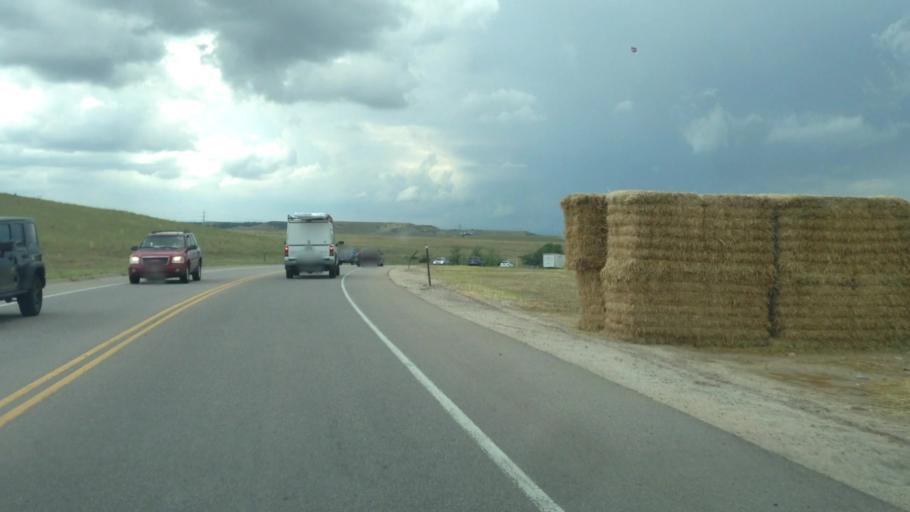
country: US
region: Colorado
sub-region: Douglas County
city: Stonegate
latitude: 39.5197
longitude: -104.8343
